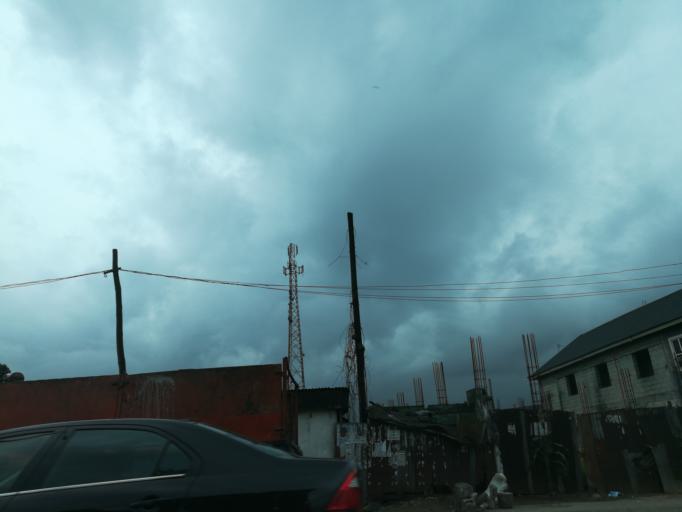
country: NG
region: Rivers
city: Port Harcourt
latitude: 4.8421
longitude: 7.0388
